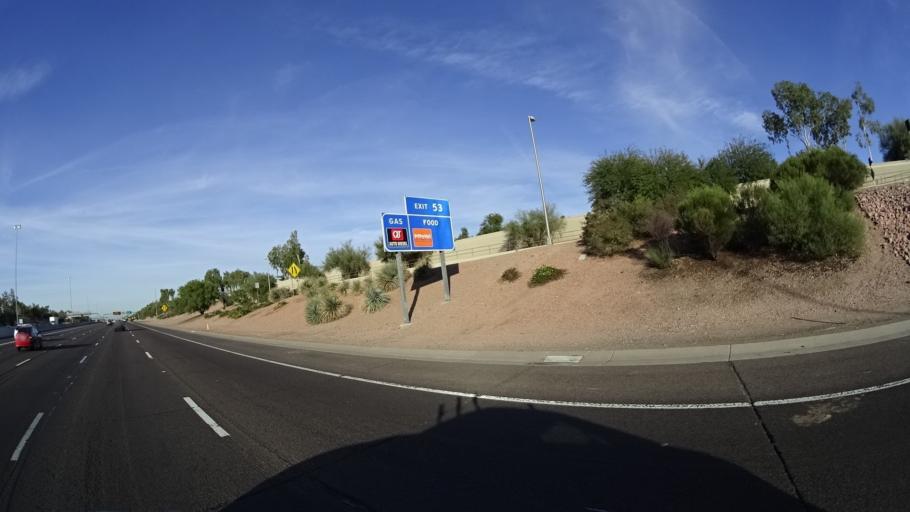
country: US
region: Arizona
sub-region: Maricopa County
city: Tempe
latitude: 33.3954
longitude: -111.8908
